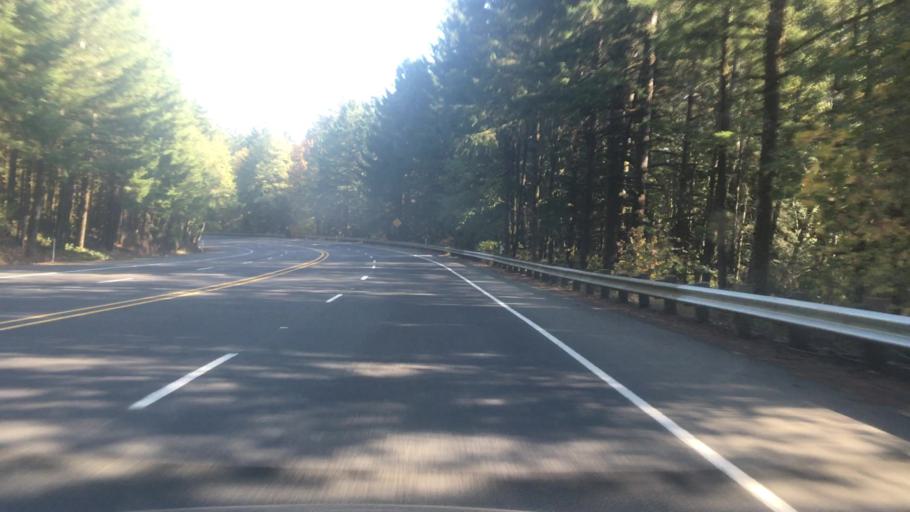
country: US
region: Oregon
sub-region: Polk County
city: Grand Ronde
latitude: 45.0578
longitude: -123.6824
